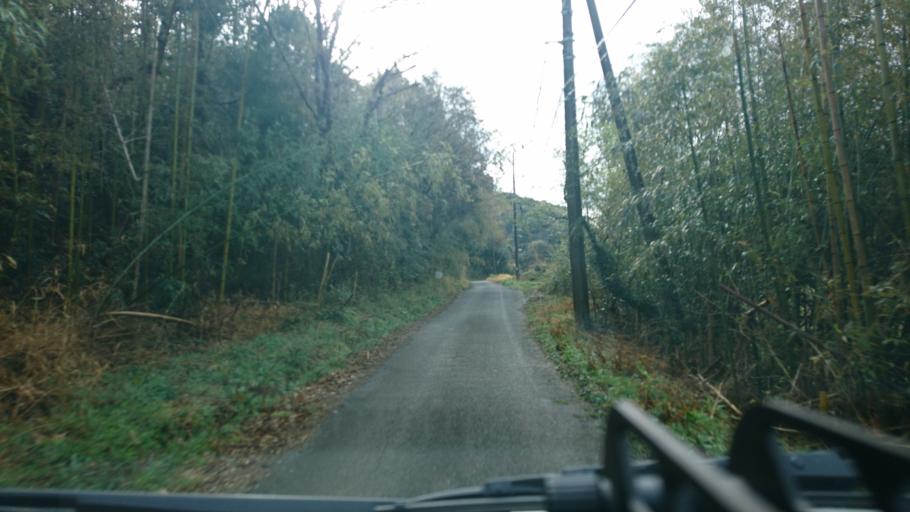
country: JP
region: Chiba
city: Kisarazu
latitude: 35.3241
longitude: 139.9675
